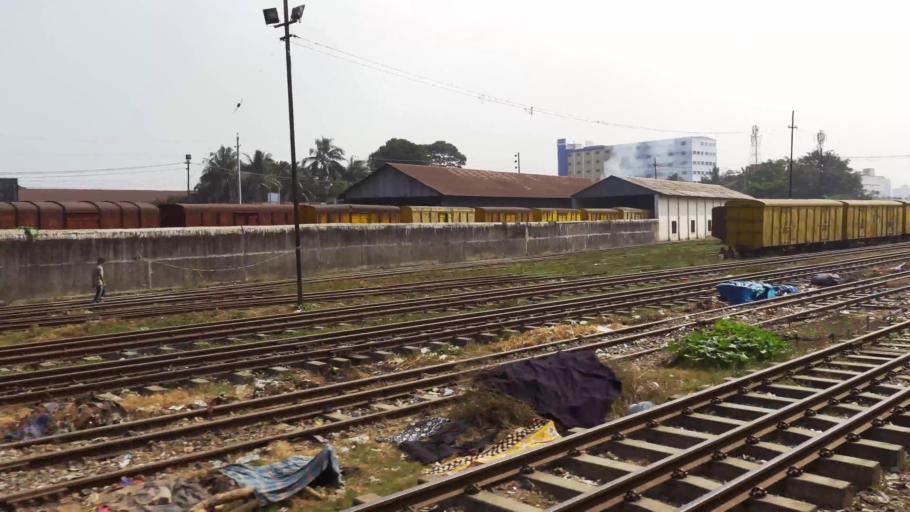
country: BD
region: Dhaka
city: Paltan
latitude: 23.7989
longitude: 90.4012
